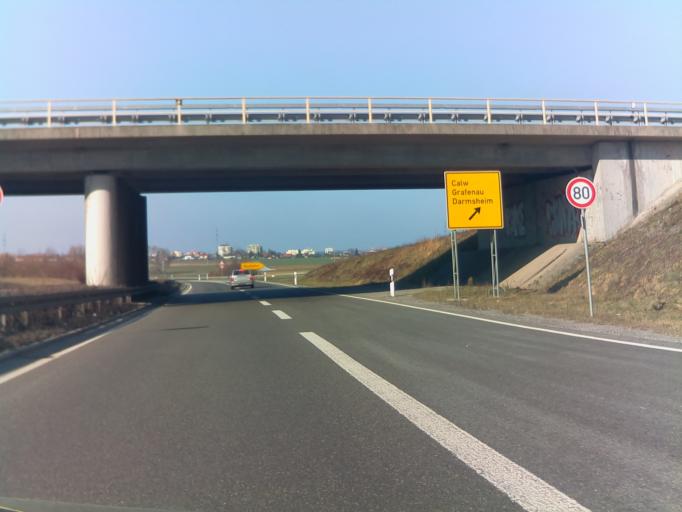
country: DE
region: Baden-Wuerttemberg
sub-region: Regierungsbezirk Stuttgart
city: Magstadt
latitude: 48.7004
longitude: 8.9663
